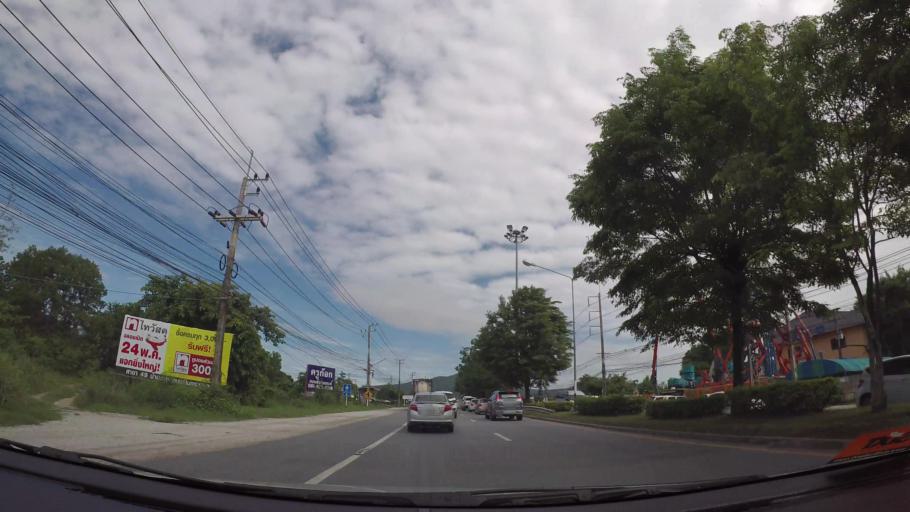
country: TH
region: Rayong
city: Ban Chang
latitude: 12.7392
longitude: 101.1240
